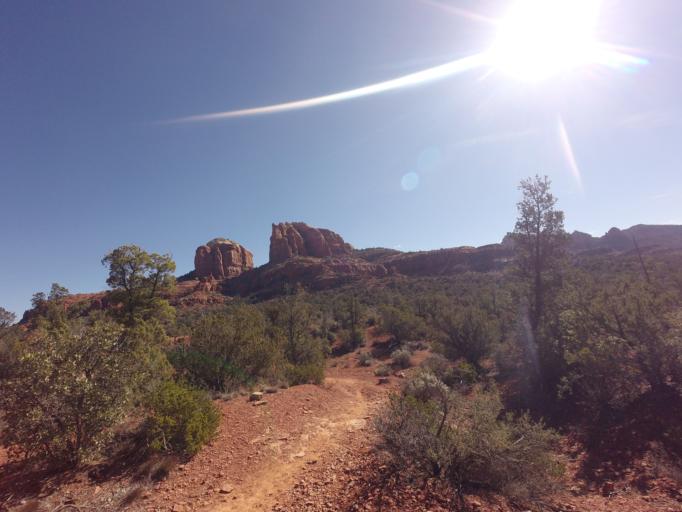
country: US
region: Arizona
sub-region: Yavapai County
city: West Sedona
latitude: 34.8159
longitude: -111.8016
